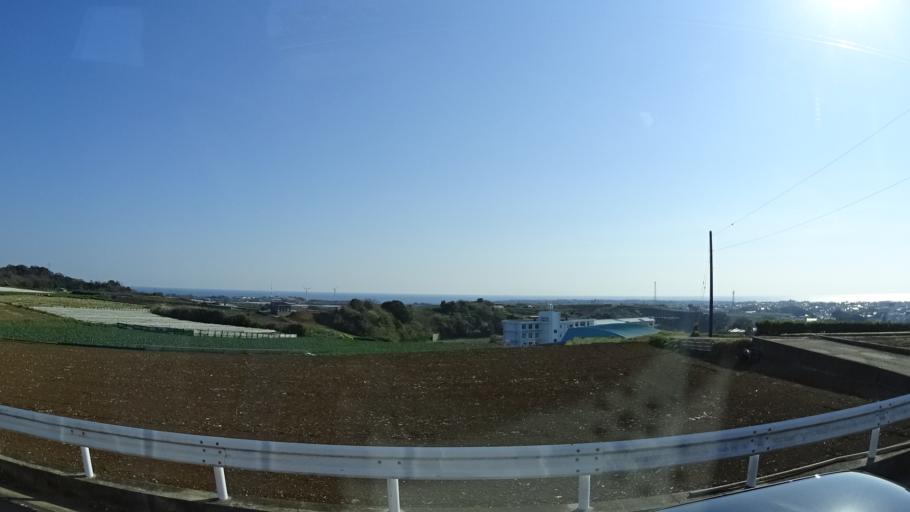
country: JP
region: Kanagawa
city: Miura
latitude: 35.1577
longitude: 139.6414
